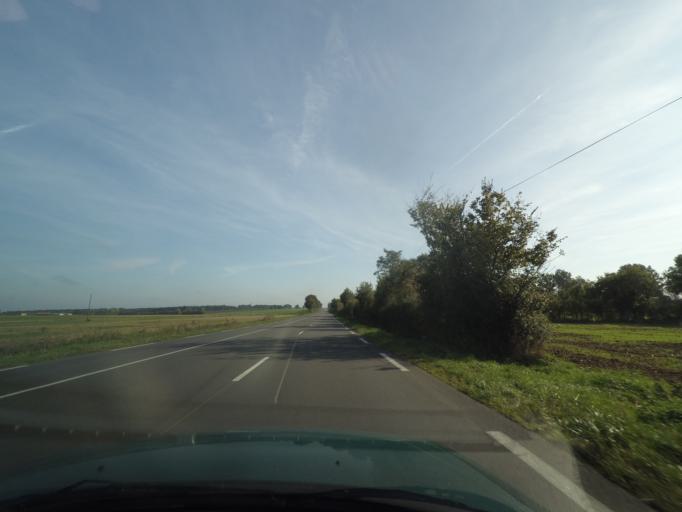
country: FR
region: Pays de la Loire
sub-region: Departement de Maine-et-Loire
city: Nueil-sur-Layon
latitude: 47.1627
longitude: -0.3929
